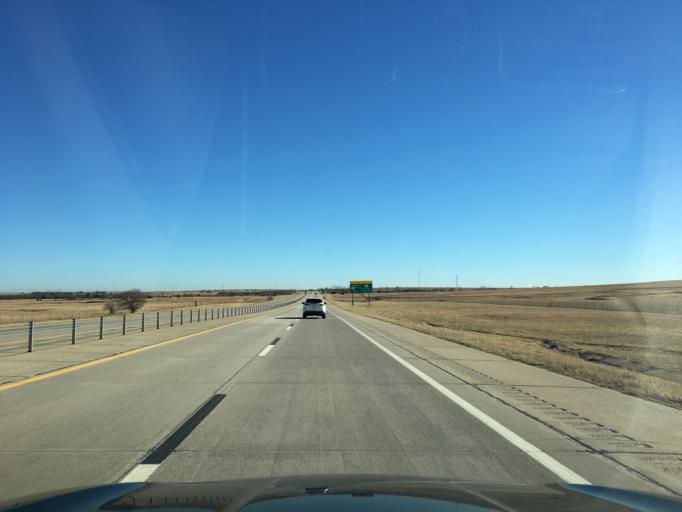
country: US
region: Oklahoma
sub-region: Noble County
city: Perry
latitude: 36.3899
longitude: -97.0969
